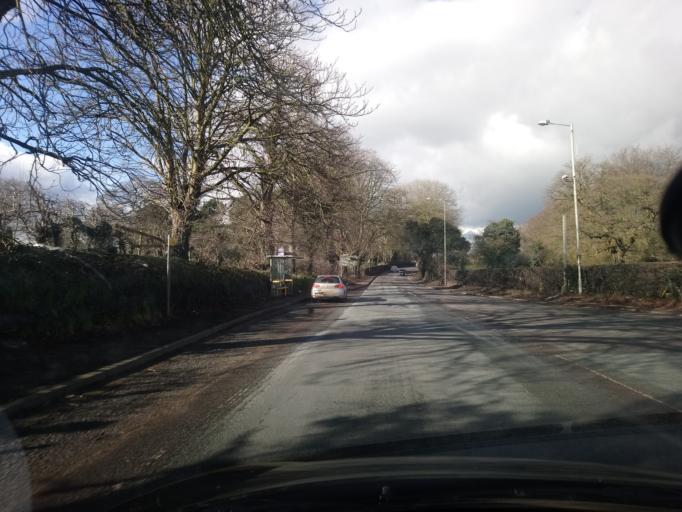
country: GB
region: England
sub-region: Cheshire West and Chester
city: Tiverton
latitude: 53.1463
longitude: -2.6613
